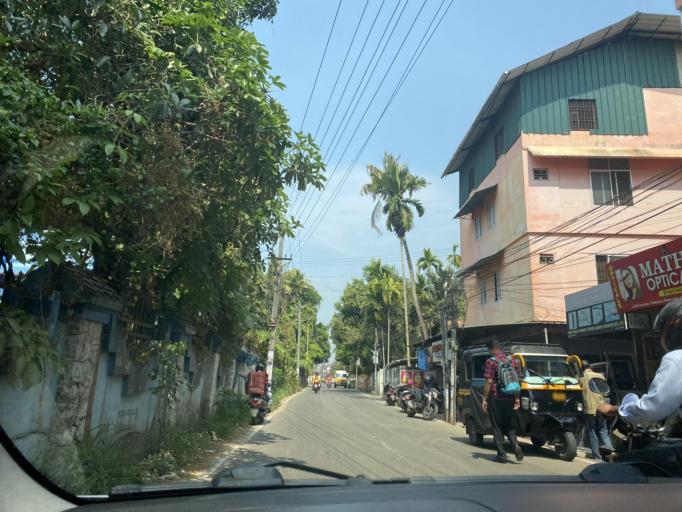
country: IN
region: Kerala
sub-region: Alappuzha
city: Arukutti
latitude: 9.9087
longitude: 76.3188
